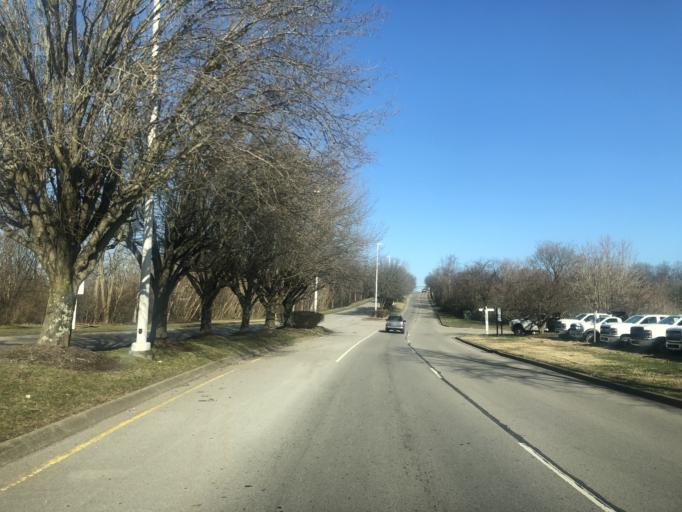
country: US
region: Tennessee
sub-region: Rutherford County
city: La Vergne
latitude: 36.0411
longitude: -86.6463
